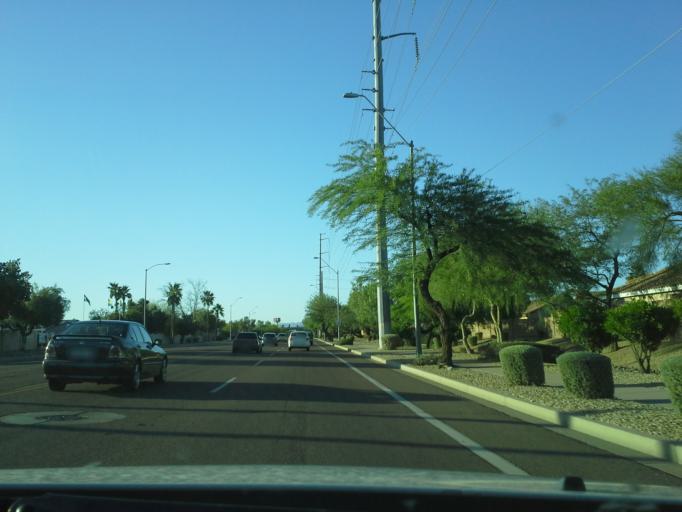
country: US
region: Arizona
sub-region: Maricopa County
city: Paradise Valley
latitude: 33.6664
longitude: -112.0136
